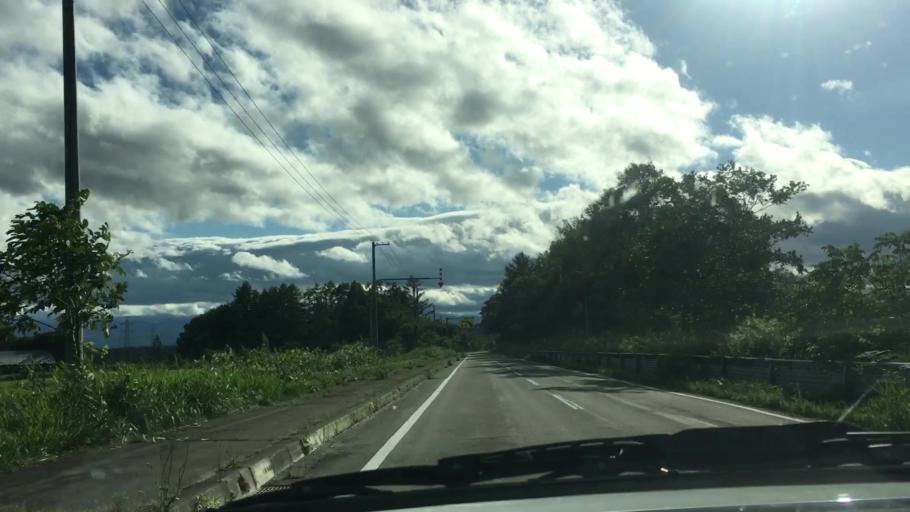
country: JP
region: Hokkaido
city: Otofuke
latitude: 43.1804
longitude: 143.0111
